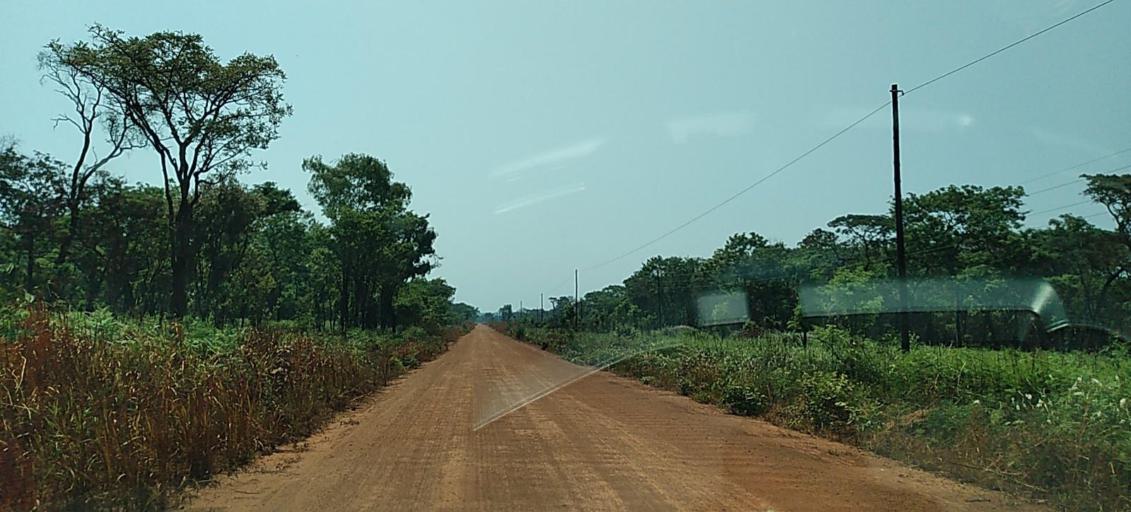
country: ZM
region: North-Western
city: Kansanshi
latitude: -11.9950
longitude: 26.6496
